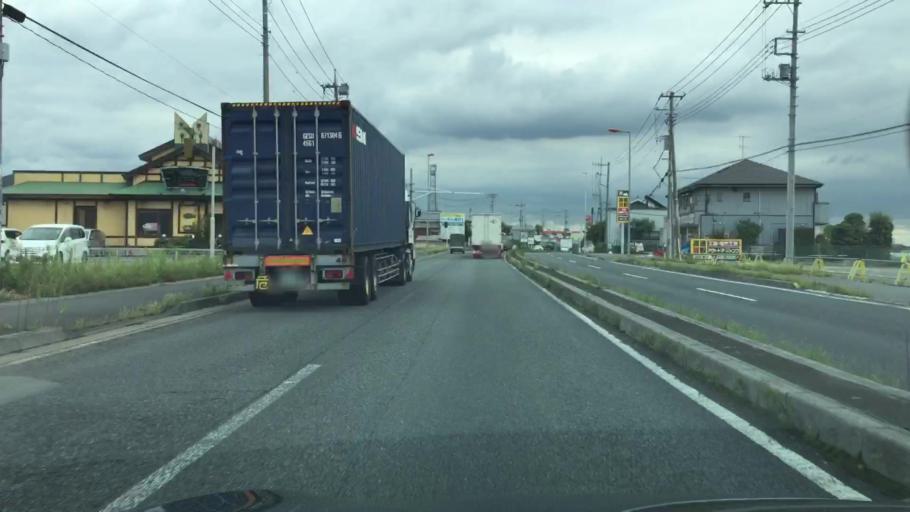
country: JP
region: Saitama
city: Kawagoe
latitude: 35.9152
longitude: 139.5259
